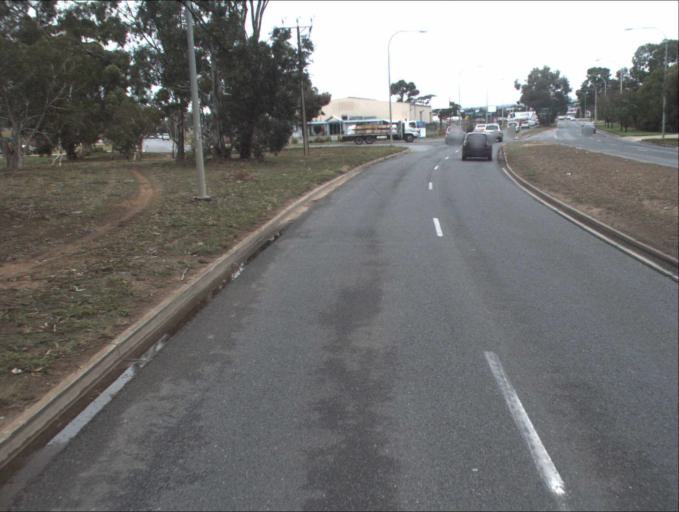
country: AU
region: South Australia
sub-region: Port Adelaide Enfield
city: Enfield
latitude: -34.8383
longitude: 138.5953
